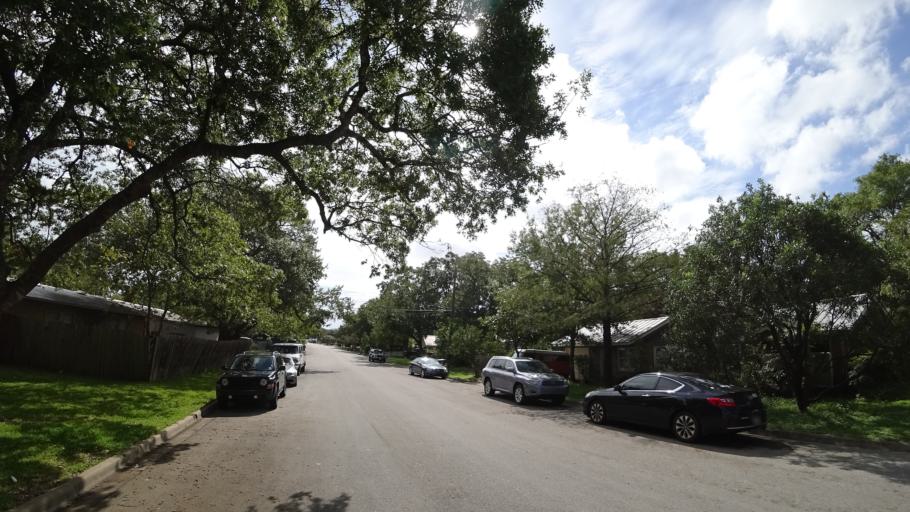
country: US
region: Texas
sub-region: Travis County
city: West Lake Hills
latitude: 30.3431
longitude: -97.7416
